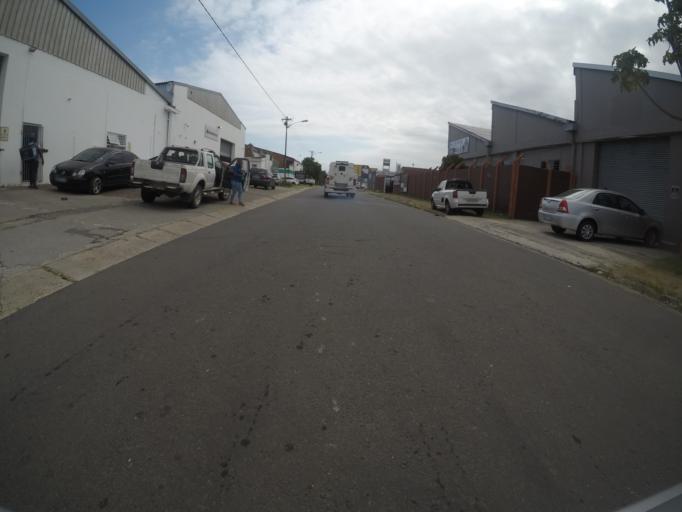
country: ZA
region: Eastern Cape
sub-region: Buffalo City Metropolitan Municipality
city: East London
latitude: -32.9865
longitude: 27.8897
